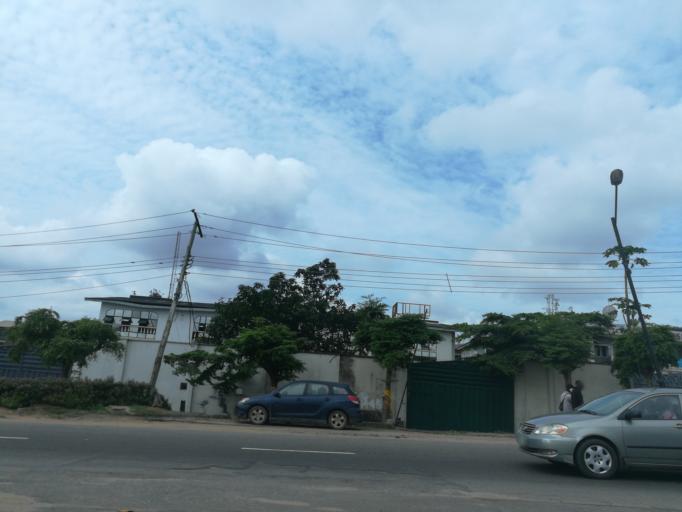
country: NG
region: Lagos
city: Somolu
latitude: 6.5563
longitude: 3.3708
